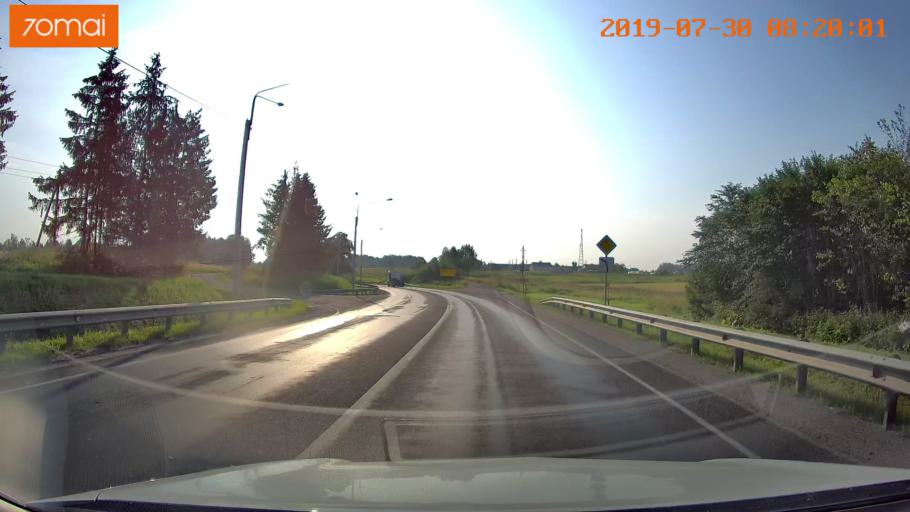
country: RU
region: Kaliningrad
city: Chernyakhovsk
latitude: 54.6258
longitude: 21.5070
